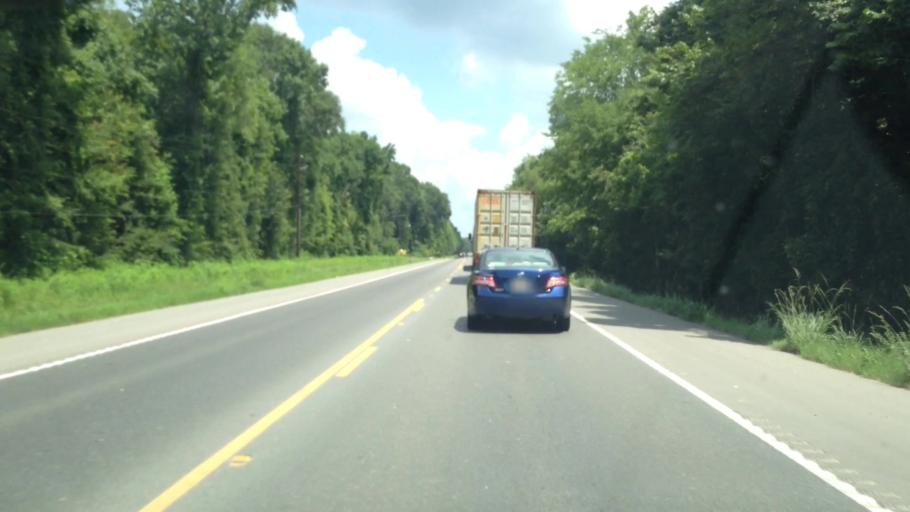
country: US
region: Louisiana
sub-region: Ascension Parish
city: Sorrento
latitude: 30.1546
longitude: -90.8756
